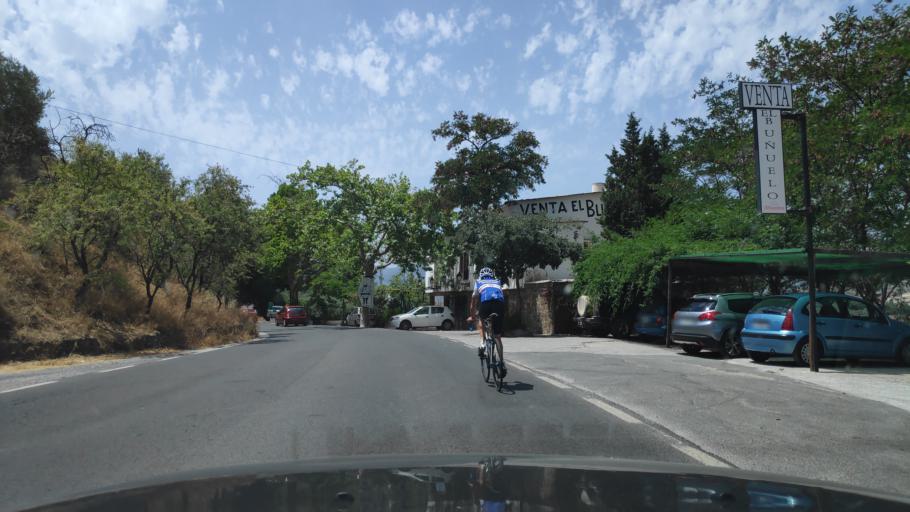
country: ES
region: Andalusia
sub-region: Provincia de Granada
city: Lanjaron
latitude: 36.9163
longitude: -3.4722
